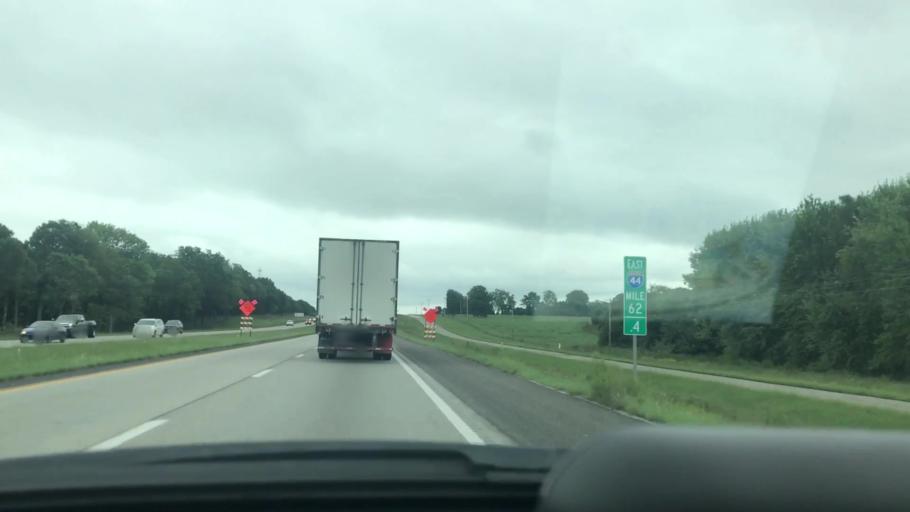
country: US
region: Missouri
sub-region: Greene County
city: Republic
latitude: 37.1858
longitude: -93.5620
